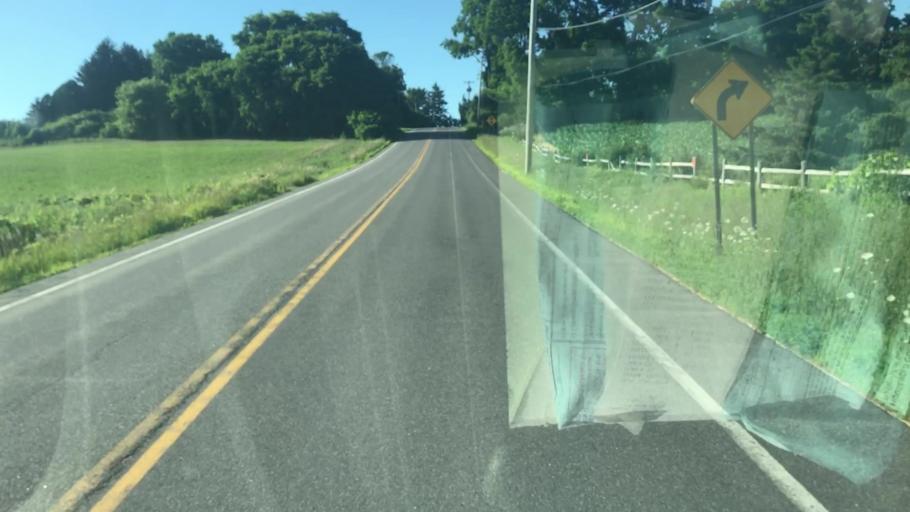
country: US
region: New York
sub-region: Onondaga County
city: Marcellus
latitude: 43.0316
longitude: -76.3640
